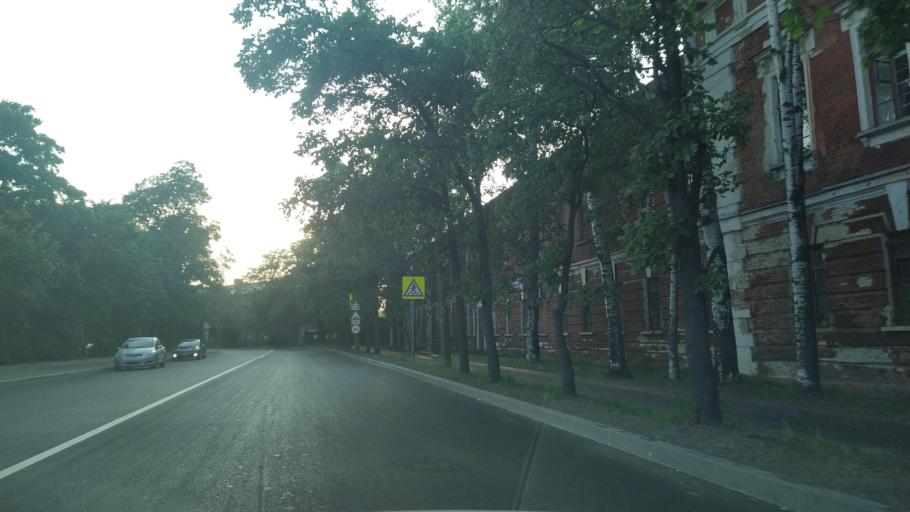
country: RU
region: St.-Petersburg
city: Kronshtadt
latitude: 60.0020
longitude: 29.7665
